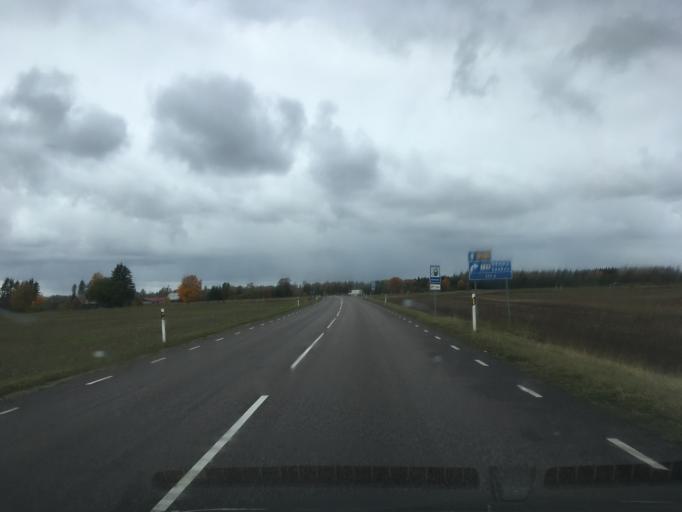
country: EE
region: Harju
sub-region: Anija vald
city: Kehra
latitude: 59.3282
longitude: 25.3238
